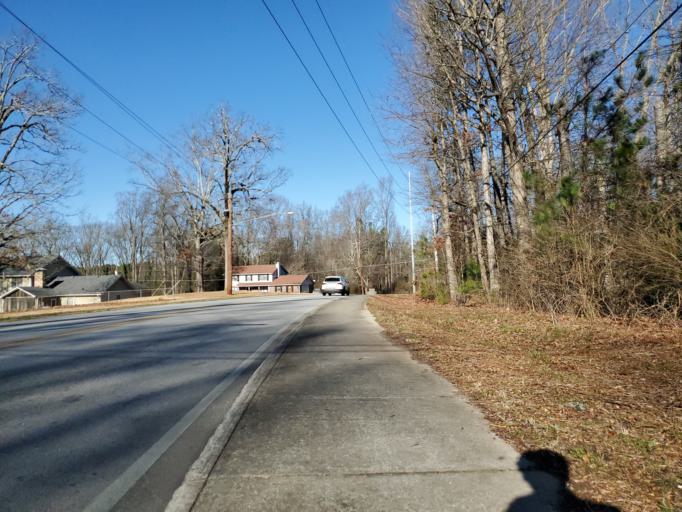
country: US
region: Georgia
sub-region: DeKalb County
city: Clarkston
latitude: 33.7728
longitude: -84.2092
